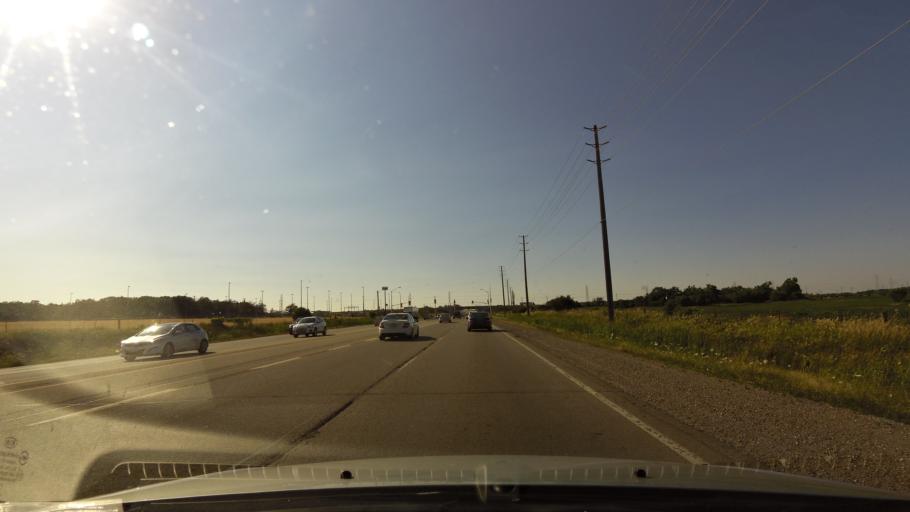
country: CA
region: Ontario
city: Oakville
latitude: 43.5050
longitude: -79.7427
